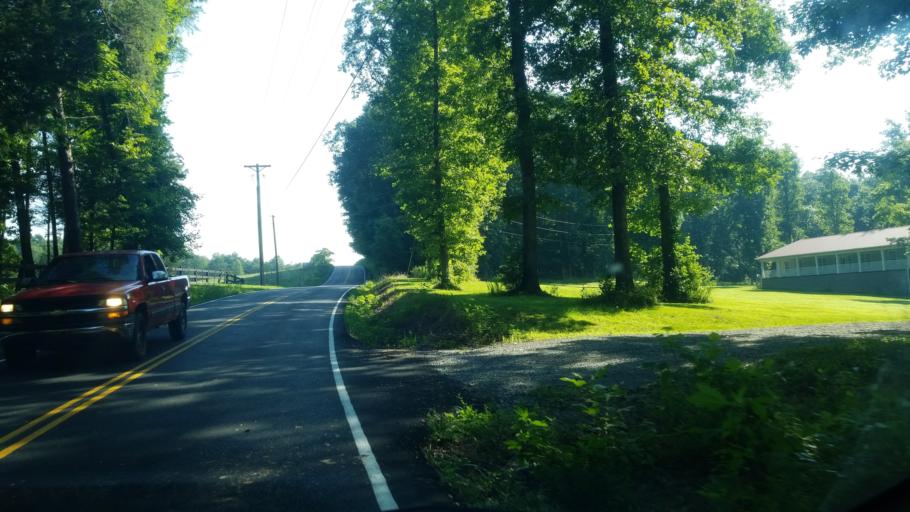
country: US
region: Tennessee
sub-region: Loudon County
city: Loudon
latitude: 35.8015
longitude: -84.3644
